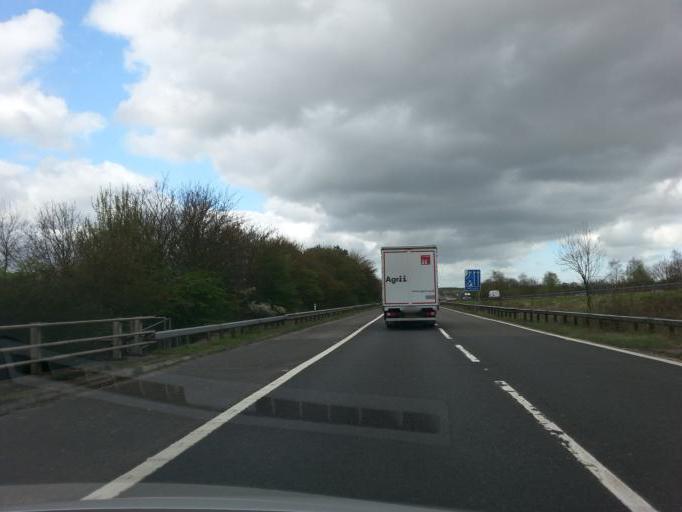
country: GB
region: England
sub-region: Hampshire
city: Overton
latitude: 51.2053
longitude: -1.1847
